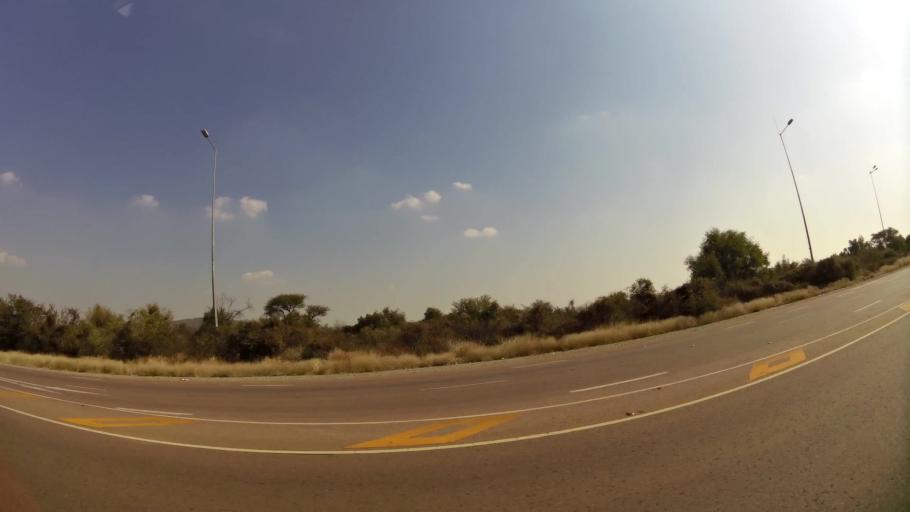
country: ZA
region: North-West
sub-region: Bojanala Platinum District Municipality
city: Mogwase
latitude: -25.4213
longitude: 27.0794
